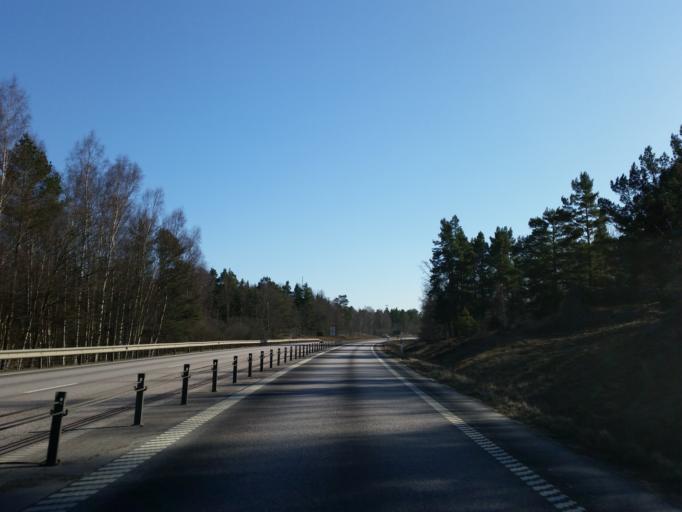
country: SE
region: Kalmar
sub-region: Oskarshamns Kommun
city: Paskallavik
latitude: 57.1824
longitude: 16.4437
